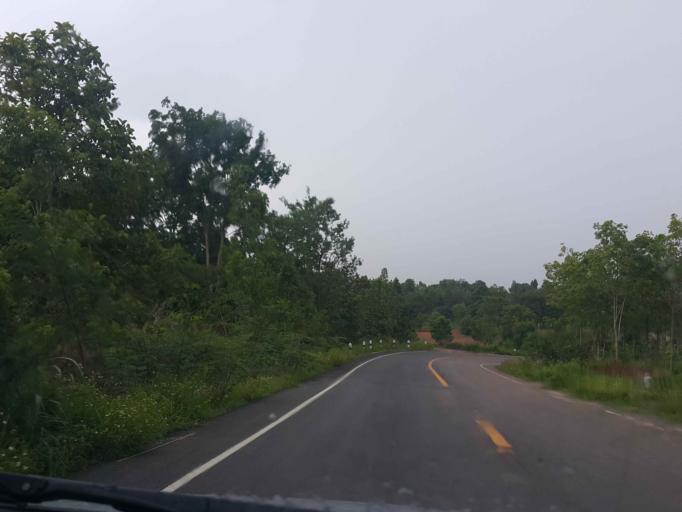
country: TH
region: Phayao
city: Dok Kham Tai
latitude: 19.0314
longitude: 99.9627
